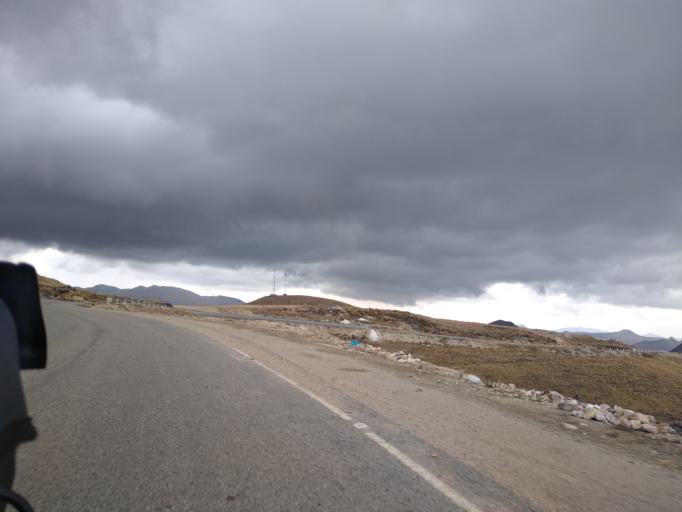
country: PE
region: La Libertad
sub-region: Provincia de Santiago de Chuco
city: Quiruvilca
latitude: -7.9933
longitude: -78.3040
